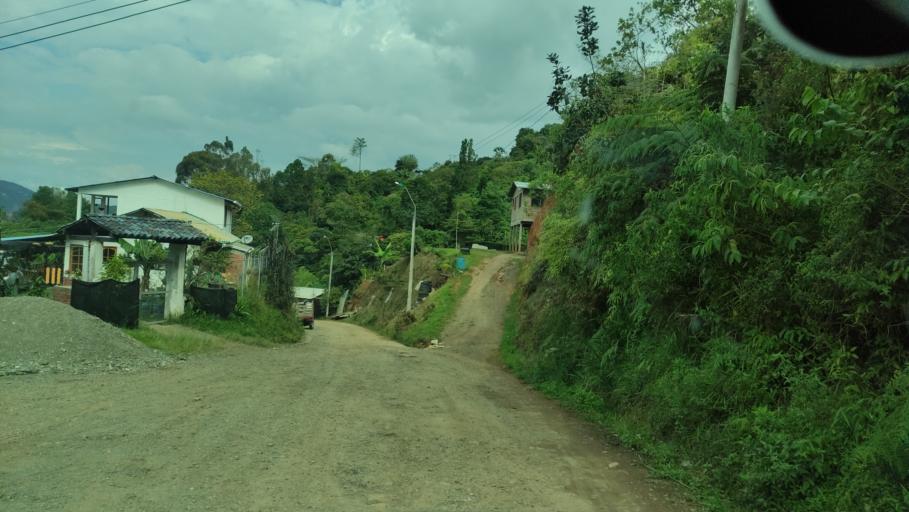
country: CO
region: Valle del Cauca
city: Cali
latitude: 3.4532
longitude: -76.6344
